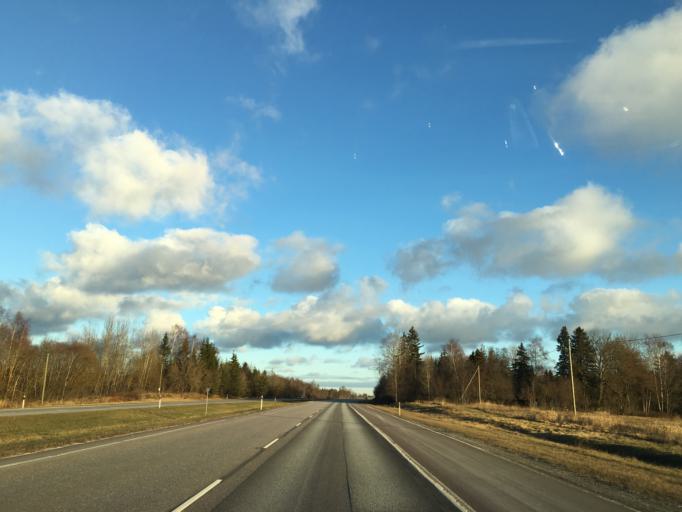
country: EE
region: Harju
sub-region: Saue linn
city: Saue
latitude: 59.2861
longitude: 24.5361
